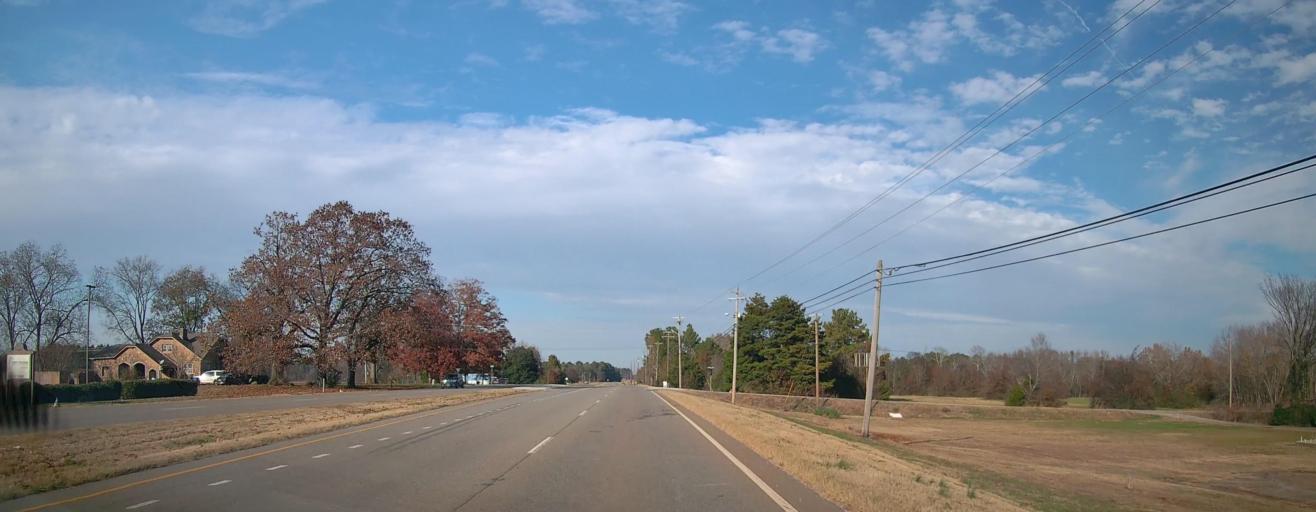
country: US
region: Alabama
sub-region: Limestone County
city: Athens
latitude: 34.7589
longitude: -86.9570
